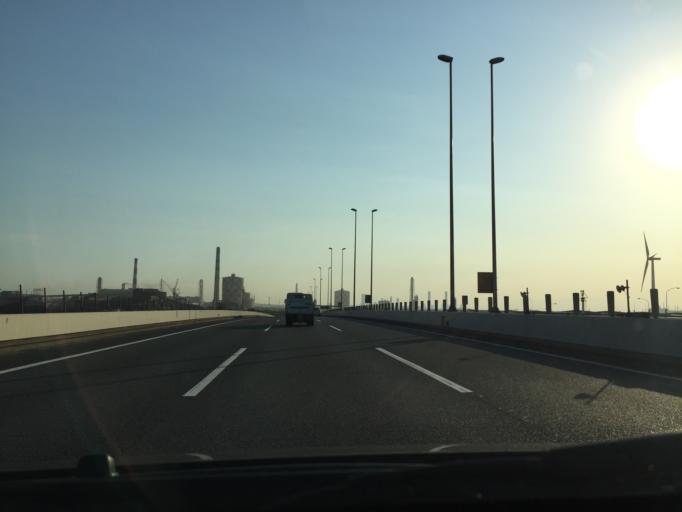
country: JP
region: Kanagawa
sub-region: Kawasaki-shi
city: Kawasaki
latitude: 35.4897
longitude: 139.7392
